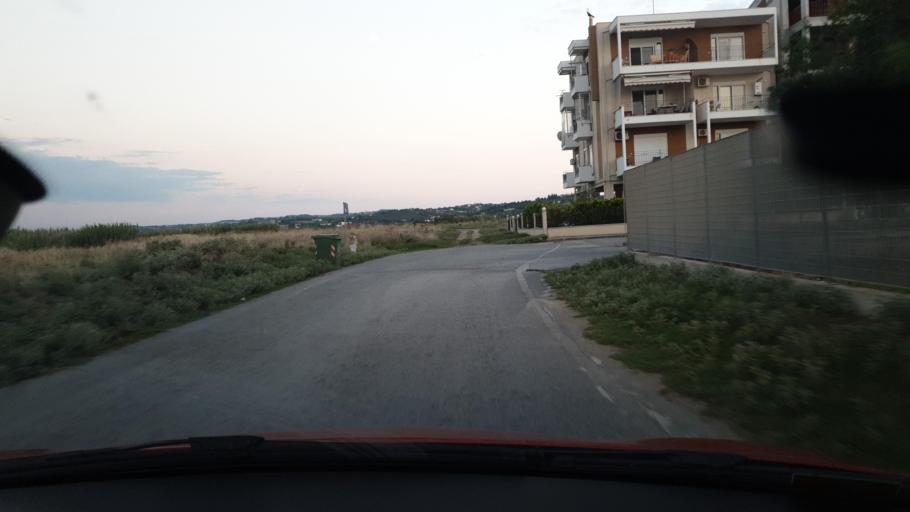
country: GR
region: Central Macedonia
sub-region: Nomos Thessalonikis
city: Peraia
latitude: 40.5124
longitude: 22.9377
